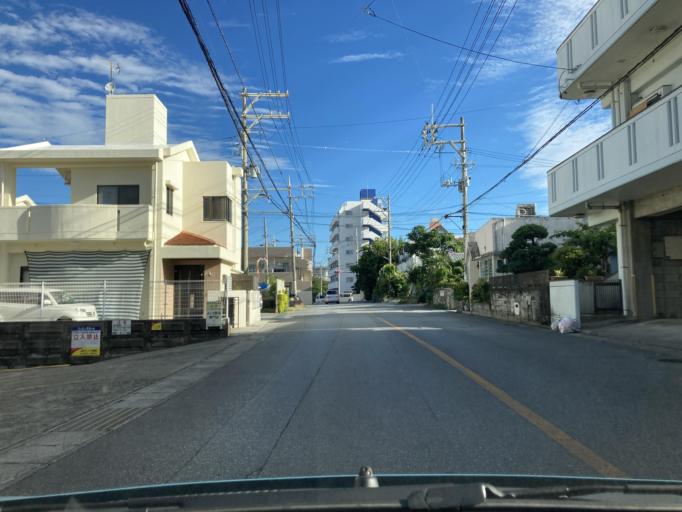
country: JP
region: Okinawa
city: Ginowan
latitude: 26.2724
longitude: 127.7407
